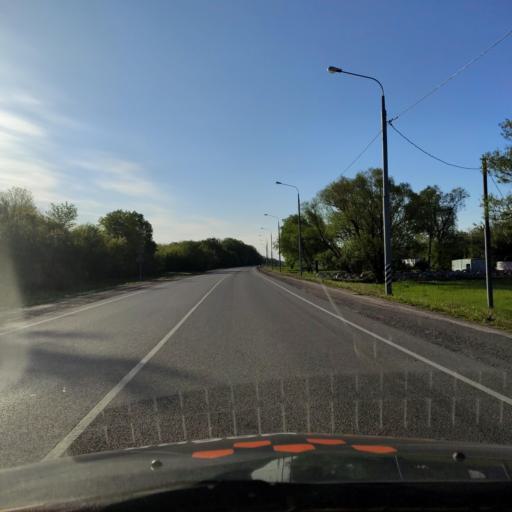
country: RU
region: Lipetsk
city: Yelets
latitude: 52.5814
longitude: 38.6326
